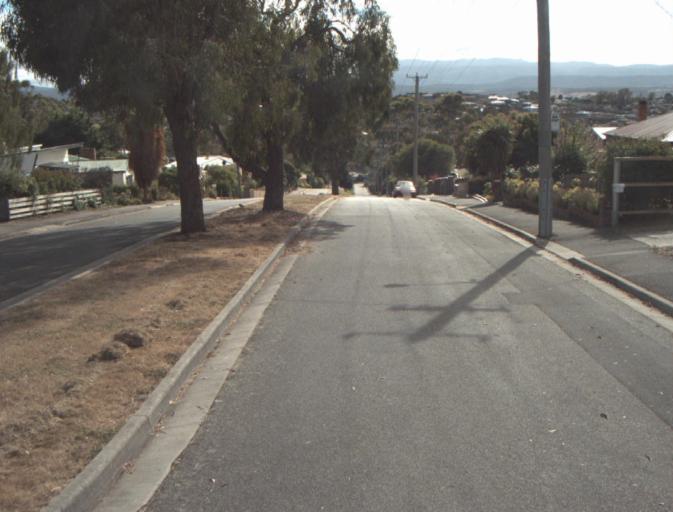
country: AU
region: Tasmania
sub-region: Launceston
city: Summerhill
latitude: -41.4654
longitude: 147.1173
